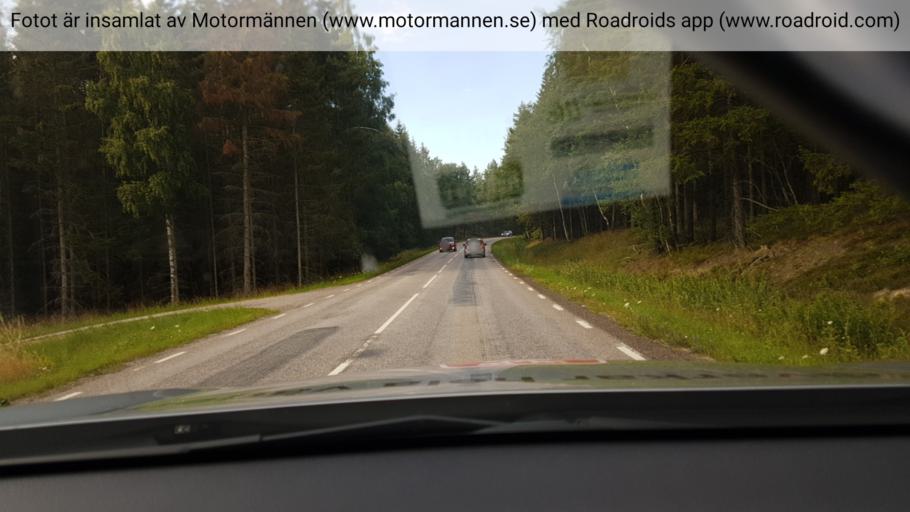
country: SE
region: Vaestra Goetaland
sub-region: Lidkopings Kommun
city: Lidkoping
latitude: 58.6070
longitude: 13.1207
